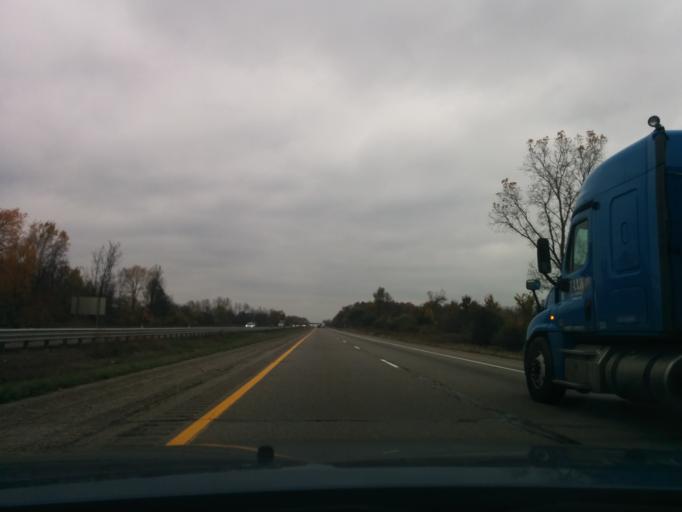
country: US
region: Michigan
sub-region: Washtenaw County
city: Ann Arbor
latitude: 42.3337
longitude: -83.7436
